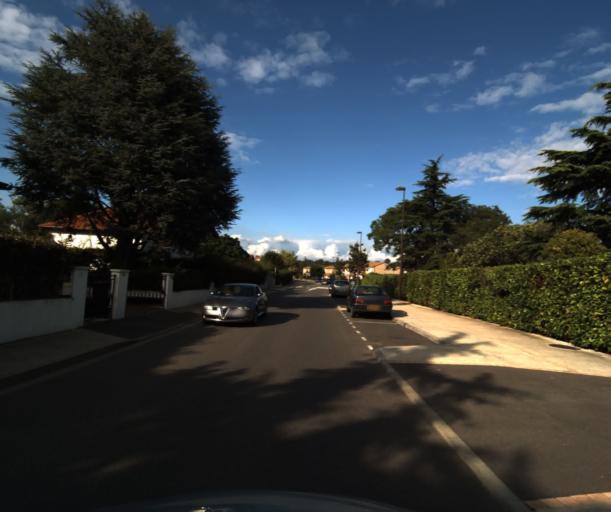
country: FR
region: Midi-Pyrenees
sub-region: Departement de la Haute-Garonne
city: Muret
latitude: 43.4661
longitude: 1.3368
